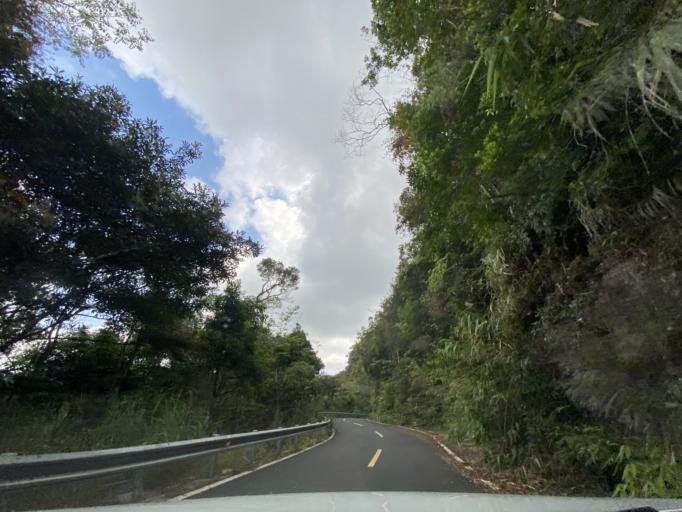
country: CN
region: Hainan
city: Diaoluoshan
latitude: 18.7127
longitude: 109.8813
